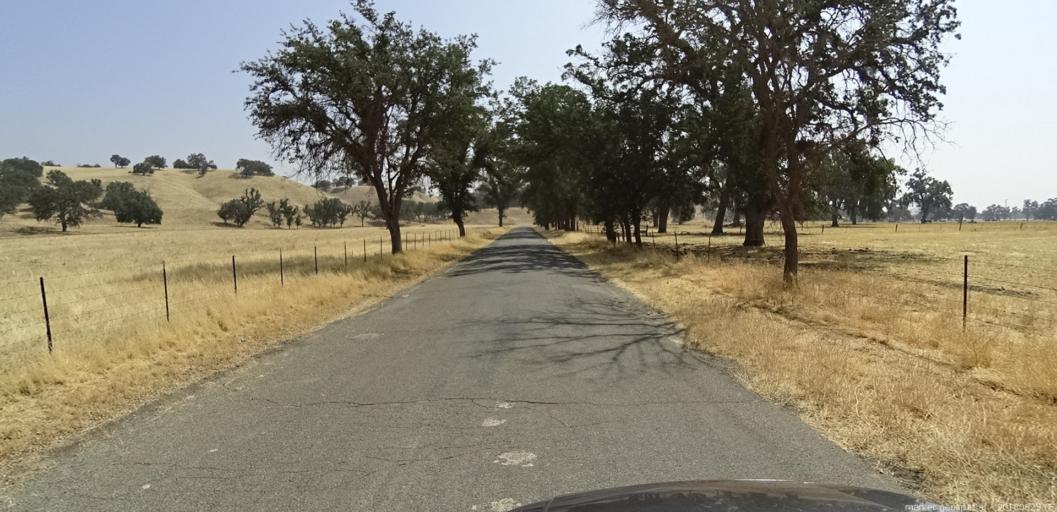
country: US
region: California
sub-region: San Luis Obispo County
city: Shandon
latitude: 35.8849
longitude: -120.4308
